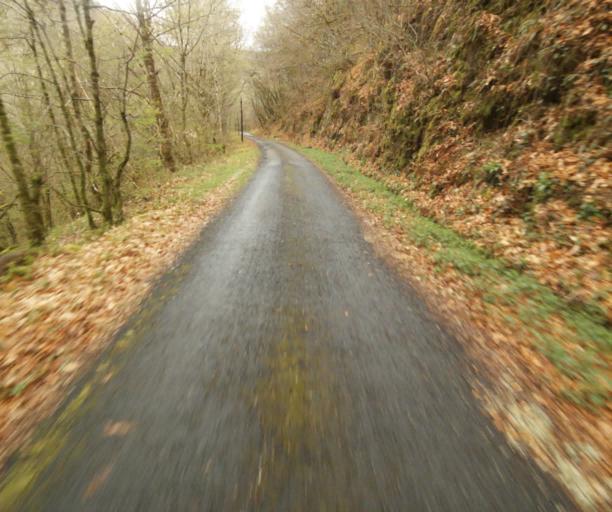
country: FR
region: Limousin
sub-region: Departement de la Correze
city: Saint-Privat
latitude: 45.2212
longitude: 2.0320
